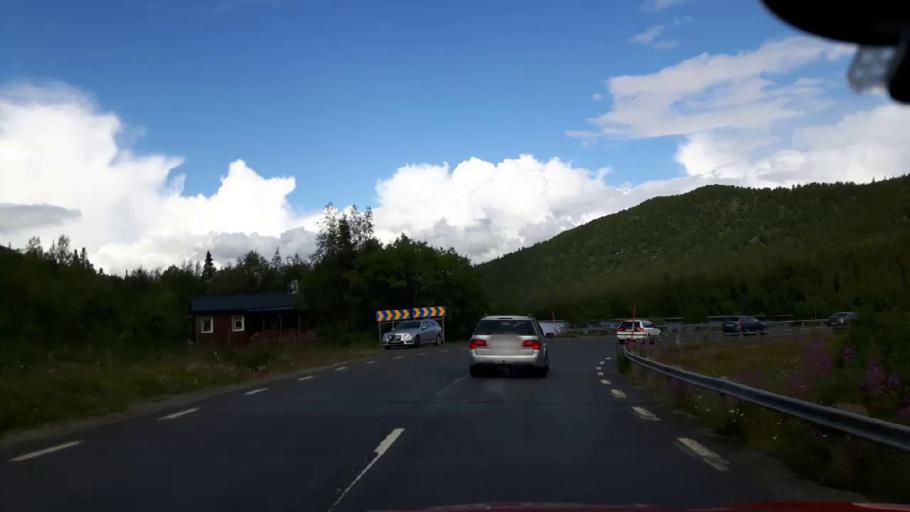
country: SE
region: Vaesterbotten
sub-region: Vilhelmina Kommun
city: Sjoberg
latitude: 65.0304
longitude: 15.1391
